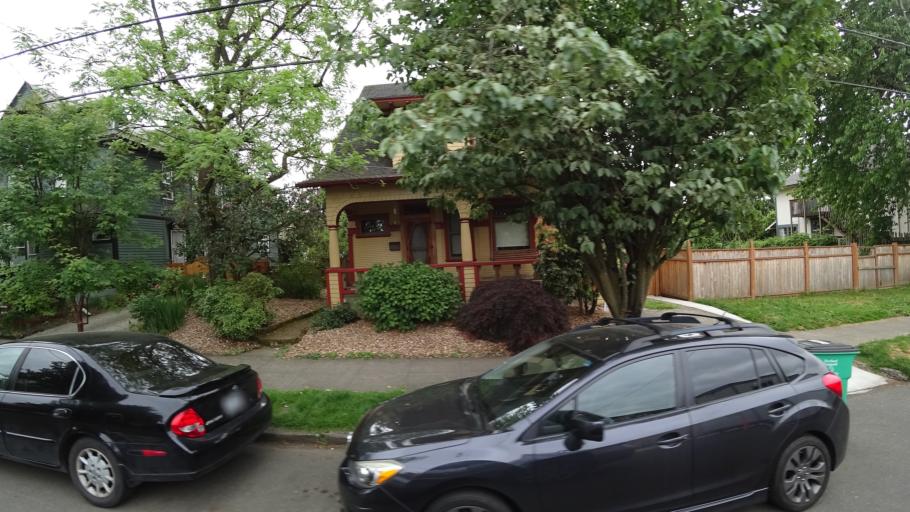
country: US
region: Oregon
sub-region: Multnomah County
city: Portland
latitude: 45.5446
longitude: -122.6605
